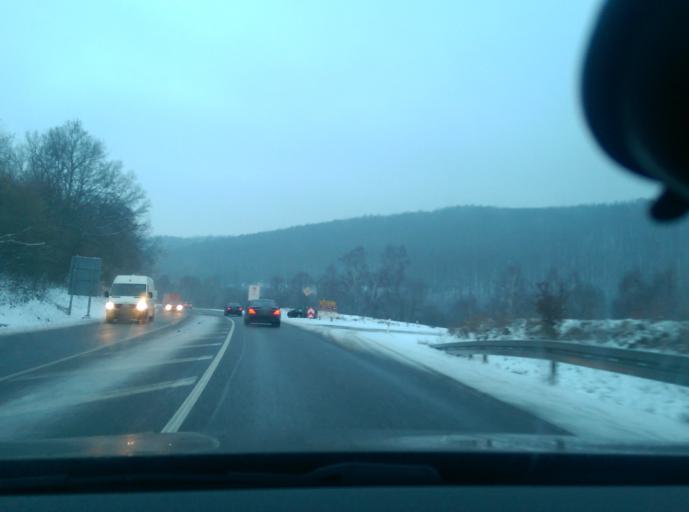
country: DE
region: Hesse
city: Waldkappel
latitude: 51.1630
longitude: 9.8523
